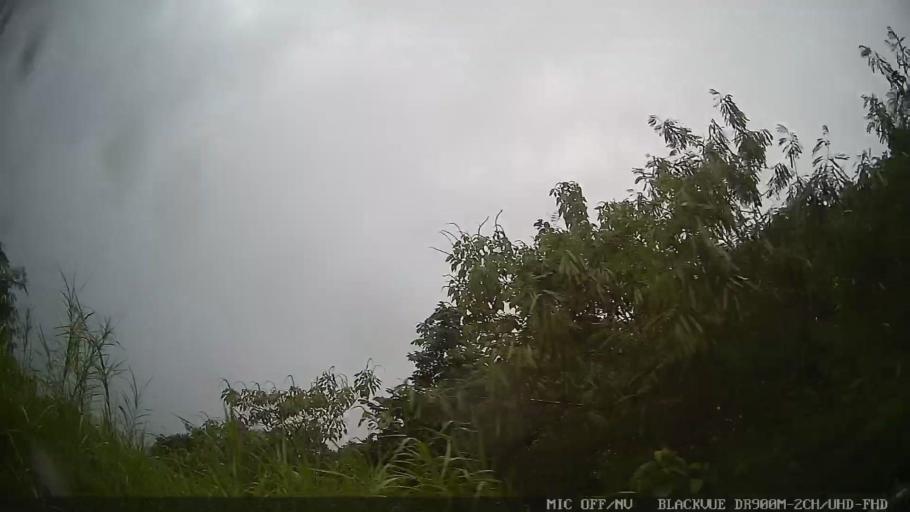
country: BR
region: Sao Paulo
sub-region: Pedreira
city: Pedreira
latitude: -22.6884
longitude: -46.8798
